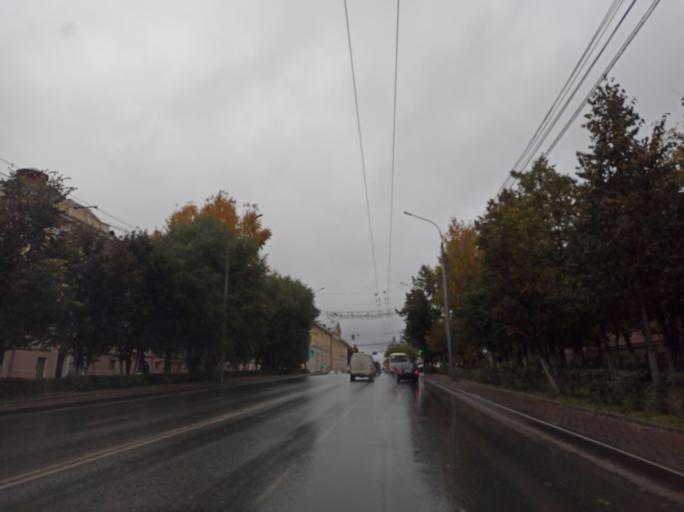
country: RU
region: Tomsk
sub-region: Tomskiy Rayon
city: Tomsk
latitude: 56.4717
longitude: 84.9506
